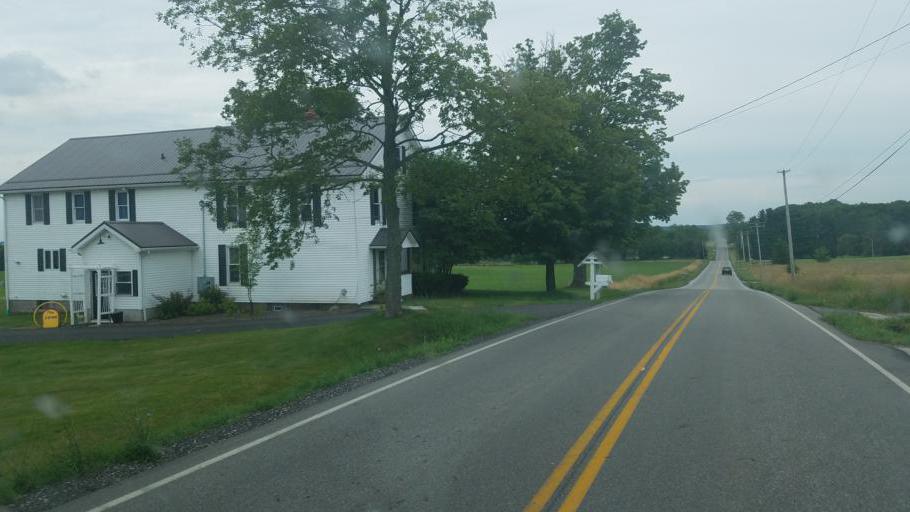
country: US
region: Ohio
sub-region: Geauga County
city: Burton
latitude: 41.4939
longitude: -81.1183
